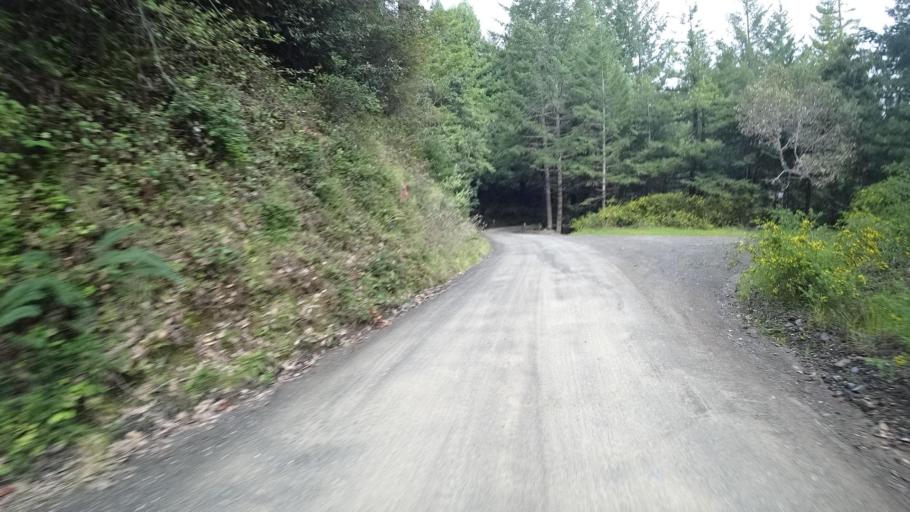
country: US
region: California
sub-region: Humboldt County
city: Redway
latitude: 40.3140
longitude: -123.8300
